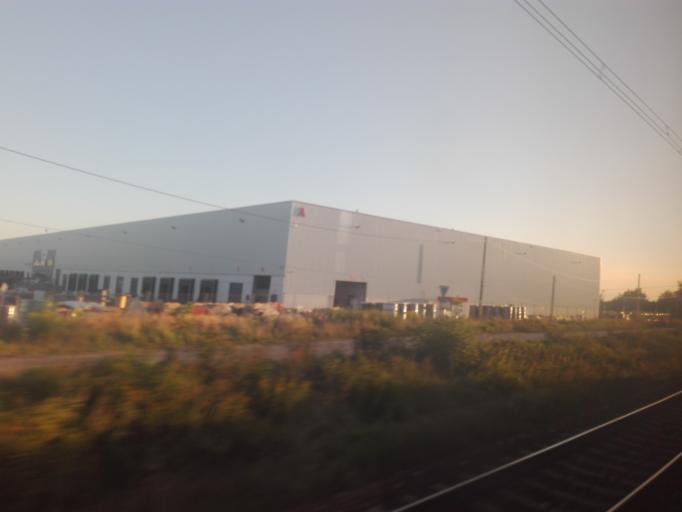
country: PL
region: Masovian Voivodeship
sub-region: Powiat warszawski zachodni
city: Ozarow Mazowiecki
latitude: 52.2083
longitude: 20.7671
